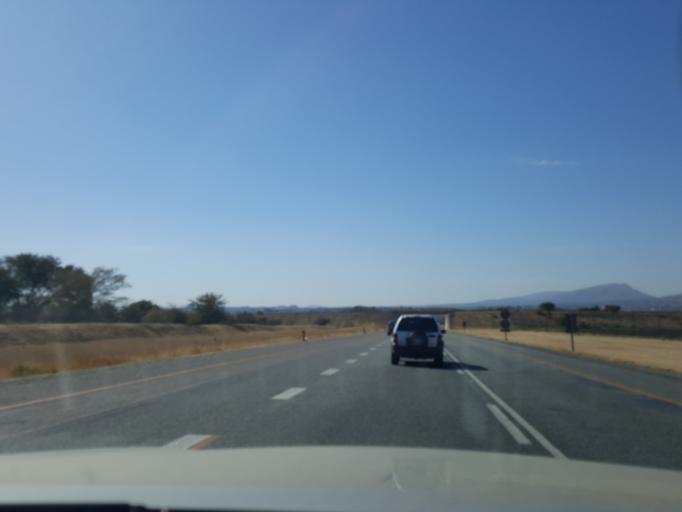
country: ZA
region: North-West
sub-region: Bojanala Platinum District Municipality
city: Brits
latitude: -25.6829
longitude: 27.7902
